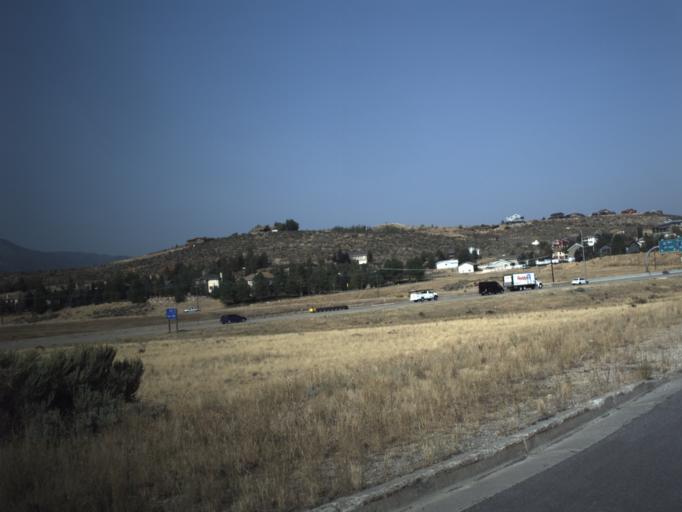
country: US
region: Utah
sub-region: Summit County
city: Snyderville
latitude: 40.7190
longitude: -111.4860
